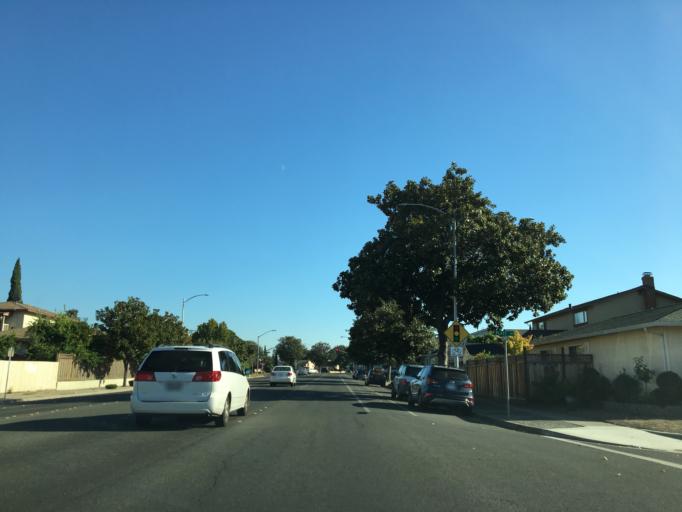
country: US
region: California
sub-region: Santa Clara County
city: Milpitas
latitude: 37.4244
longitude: -121.8787
